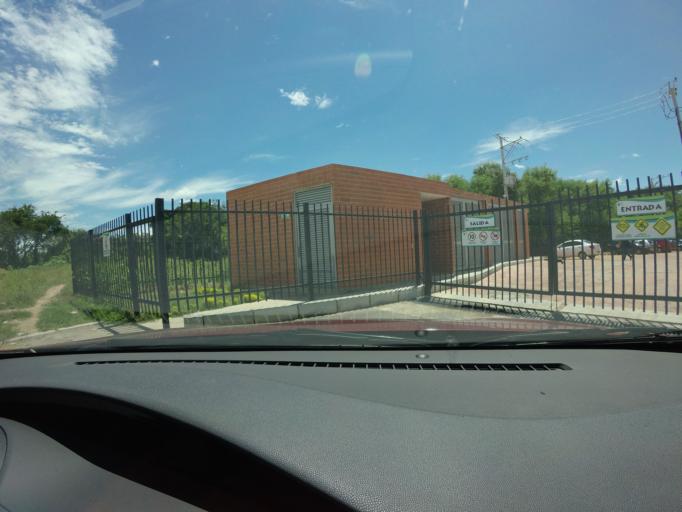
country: CO
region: Cundinamarca
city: Ricaurte
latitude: 4.2712
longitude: -74.7759
